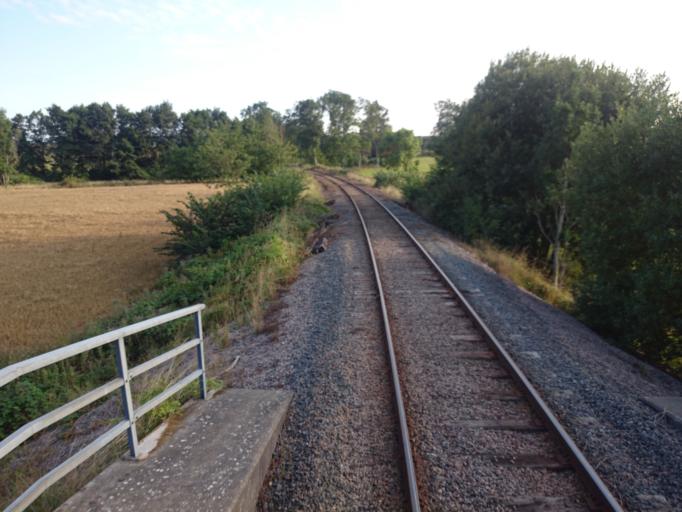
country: SE
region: Skane
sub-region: Simrishamns Kommun
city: Kivik
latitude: 55.7183
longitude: 14.1408
